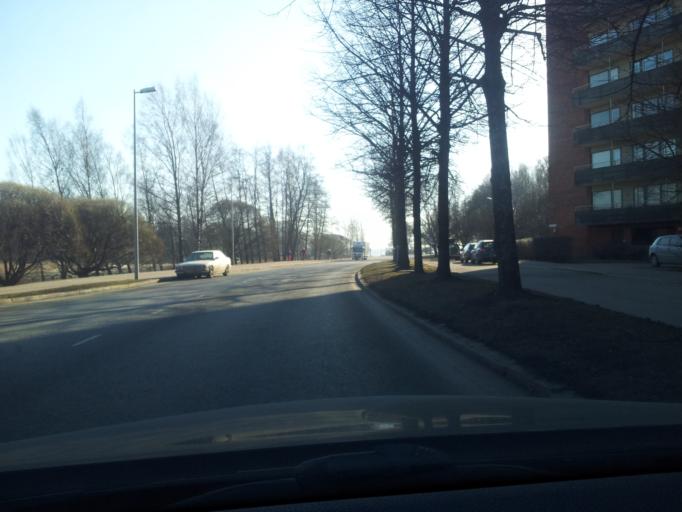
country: FI
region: Uusimaa
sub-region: Helsinki
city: Teekkarikylae
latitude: 60.1953
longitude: 24.8850
